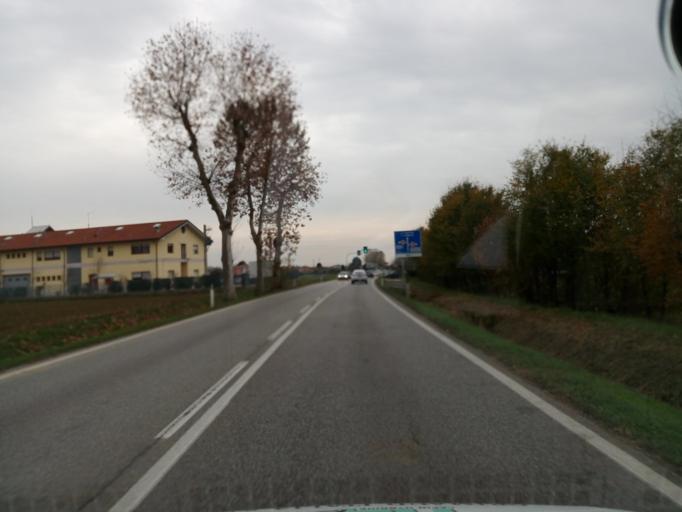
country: IT
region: Veneto
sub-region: Provincia di Treviso
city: Crocetta-Nogare
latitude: 45.8000
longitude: 12.0347
